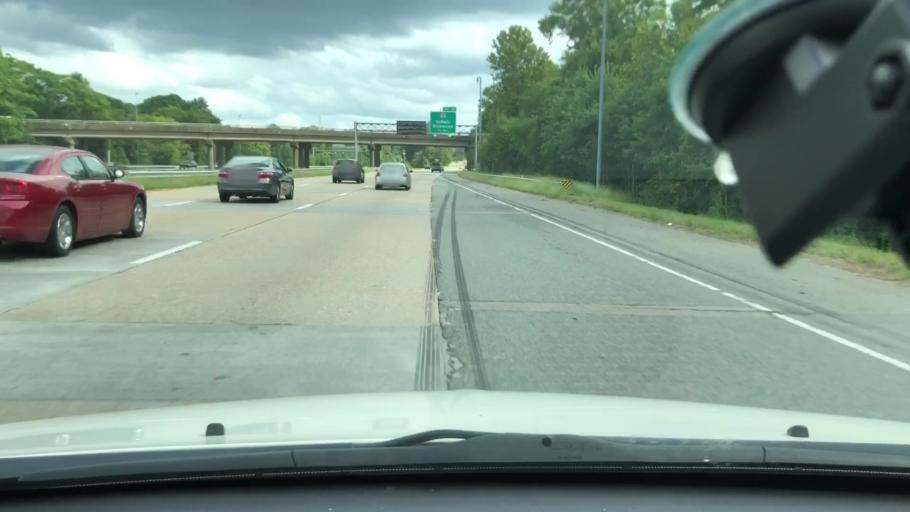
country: US
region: Virginia
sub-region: City of Chesapeake
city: Chesapeake
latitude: 36.7707
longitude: -76.2741
